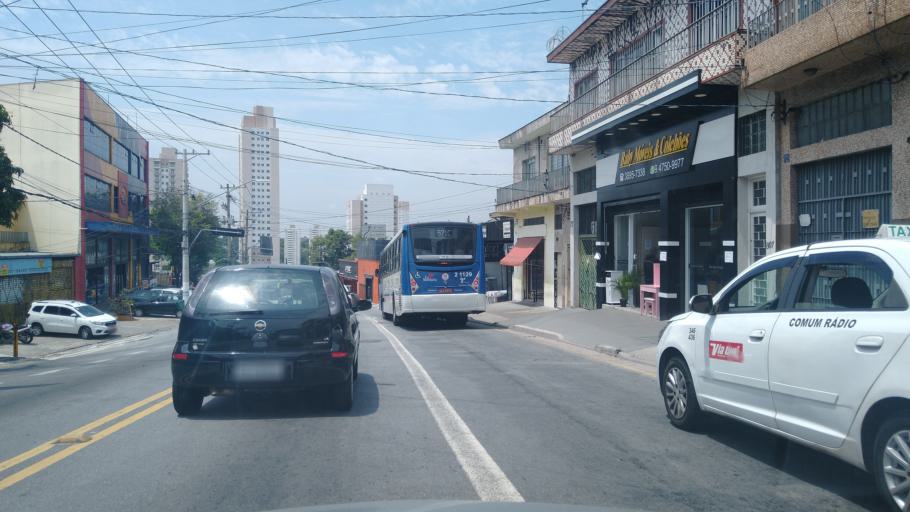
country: BR
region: Sao Paulo
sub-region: Sao Paulo
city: Sao Paulo
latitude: -23.4701
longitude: -46.6767
